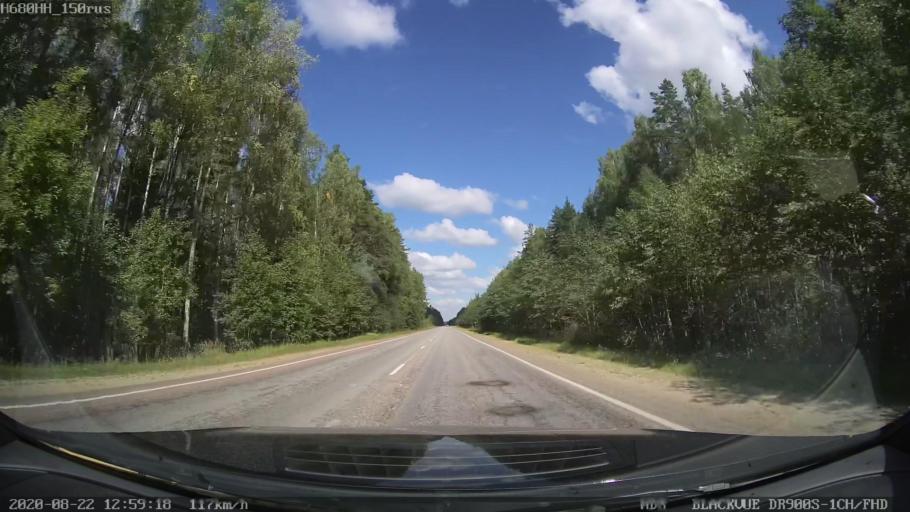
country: RU
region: Tverskaya
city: Bezhetsk
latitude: 57.6037
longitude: 36.3578
